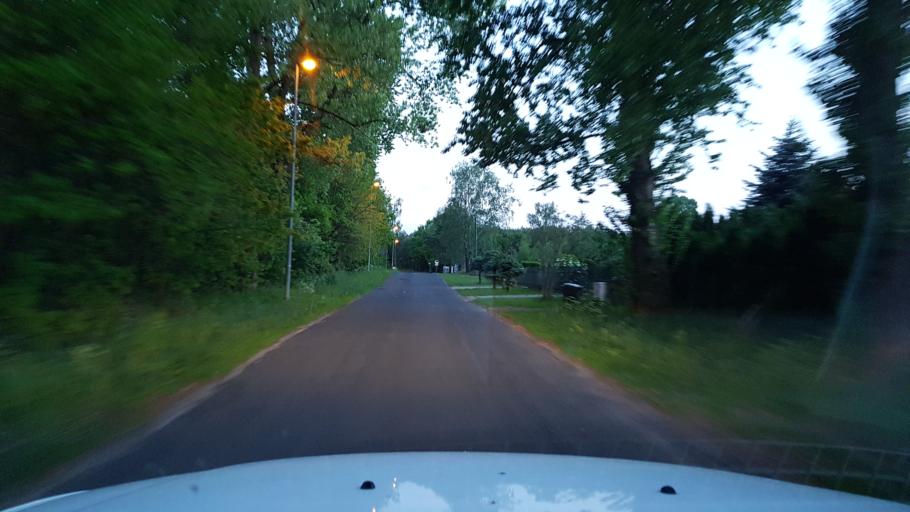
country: PL
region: West Pomeranian Voivodeship
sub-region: Powiat goleniowski
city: Mosty
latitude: 53.5039
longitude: 14.9064
